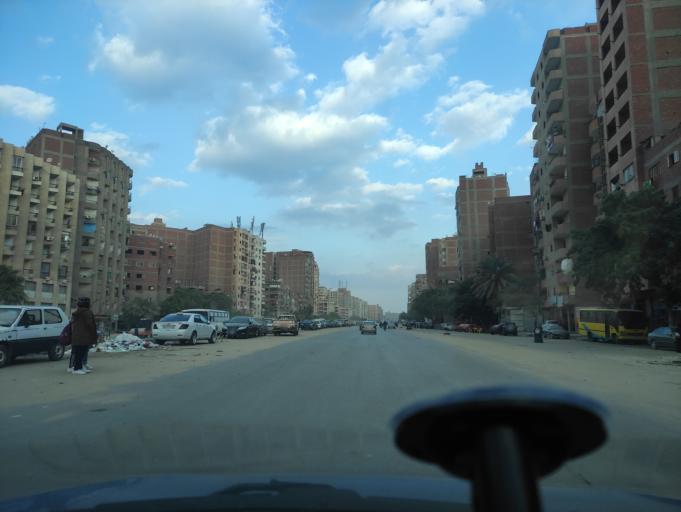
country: EG
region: Muhafazat al Qalyubiyah
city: Al Khankah
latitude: 30.1349
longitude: 31.3297
